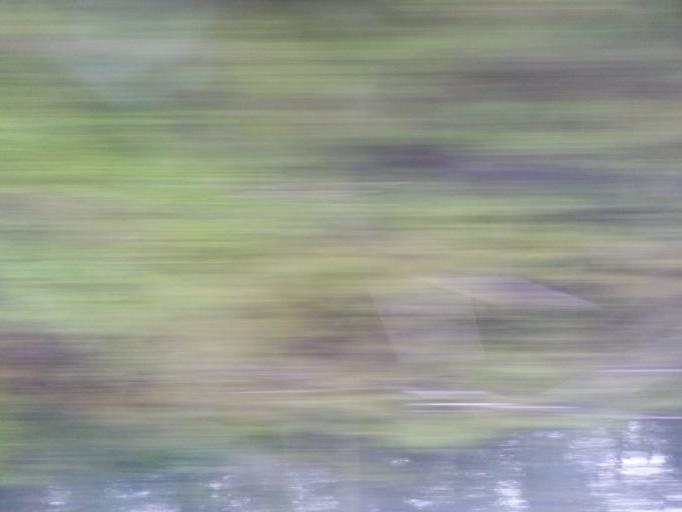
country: NO
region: Sor-Trondelag
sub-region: Rennebu
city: Berkak
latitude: 62.9058
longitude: 10.1255
